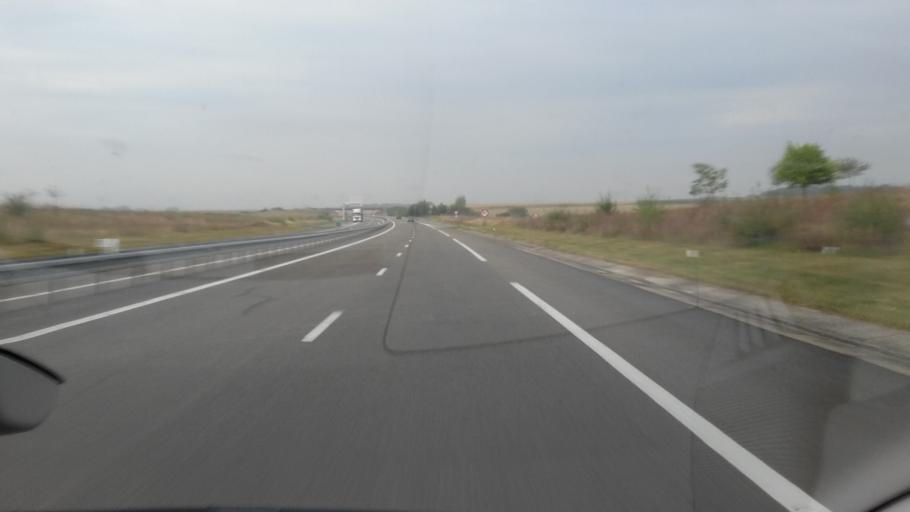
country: FR
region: Champagne-Ardenne
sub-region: Departement des Ardennes
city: Attigny
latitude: 49.5947
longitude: 4.5001
